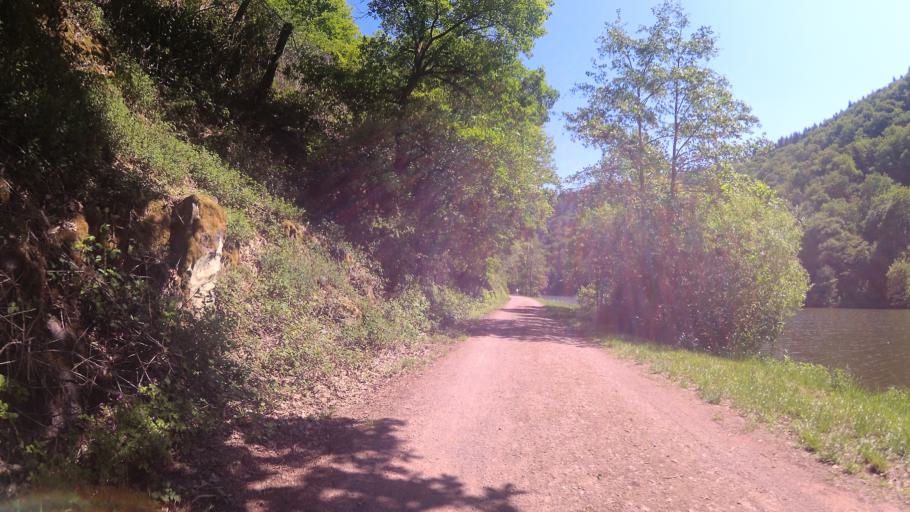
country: DE
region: Saarland
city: Mettlach
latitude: 49.4939
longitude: 6.5708
